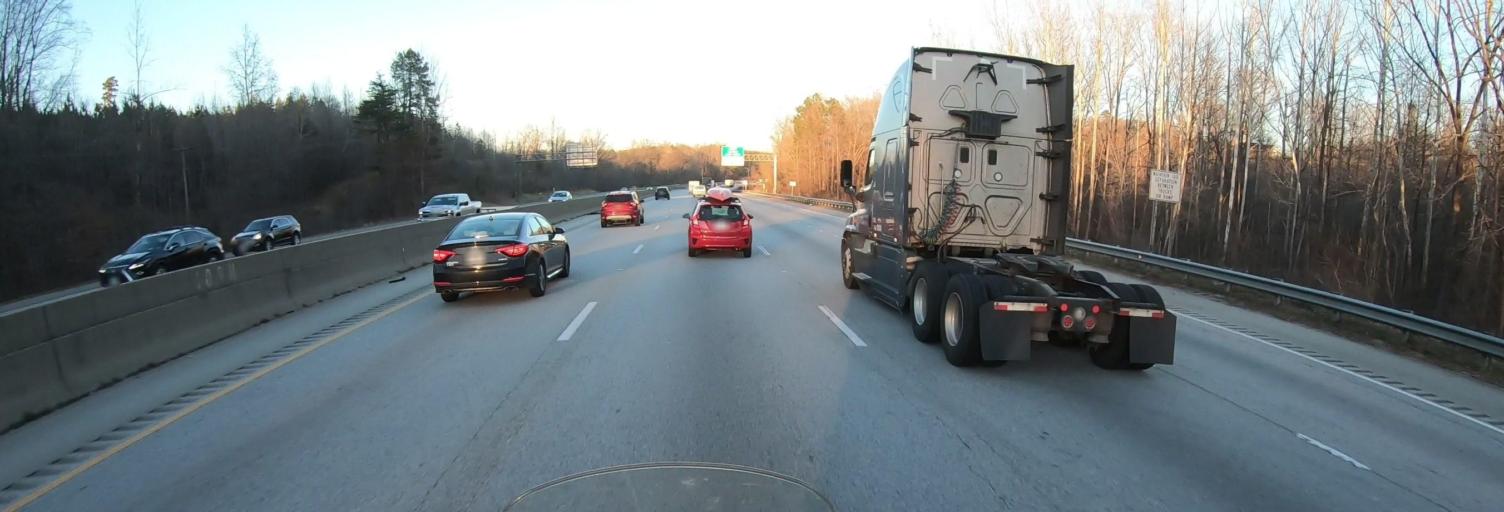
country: US
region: North Carolina
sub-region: Gaston County
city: Bessemer City
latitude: 35.2548
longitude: -81.2874
